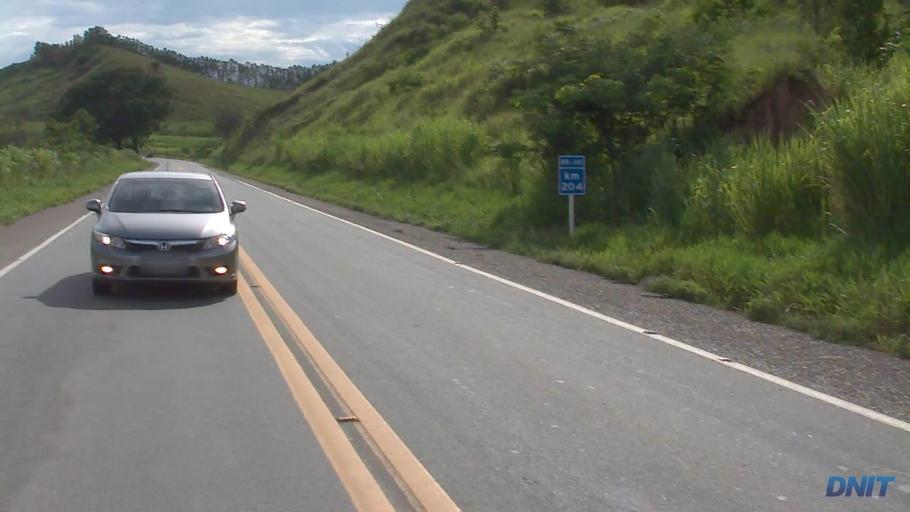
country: BR
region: Minas Gerais
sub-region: Belo Oriente
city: Belo Oriente
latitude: -19.1817
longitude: -42.2614
